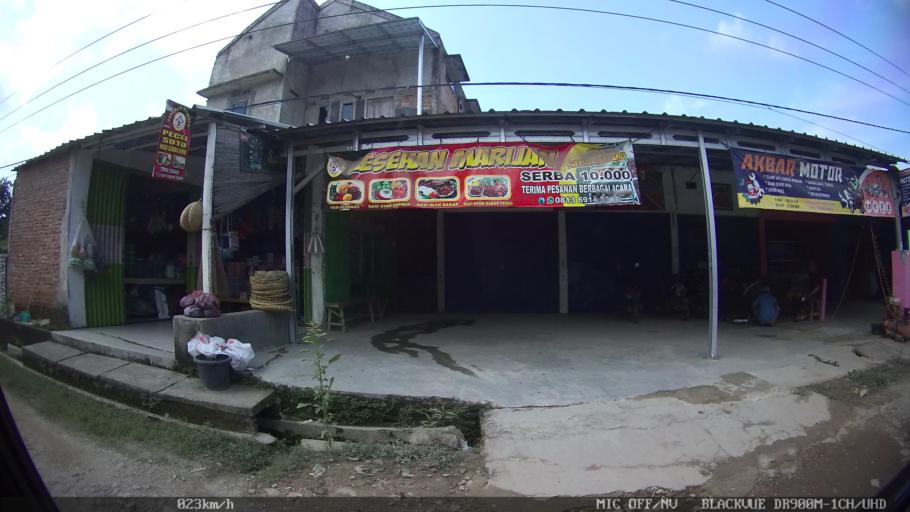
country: ID
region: Lampung
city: Kedaton
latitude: -5.3420
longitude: 105.2922
